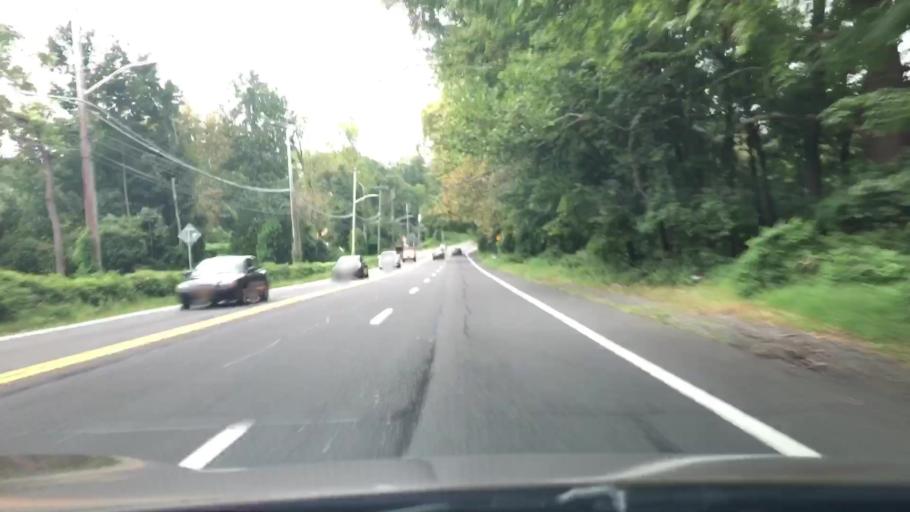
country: US
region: New York
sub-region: Westchester County
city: Sleepy Hollow
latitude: 41.1163
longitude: -73.8599
